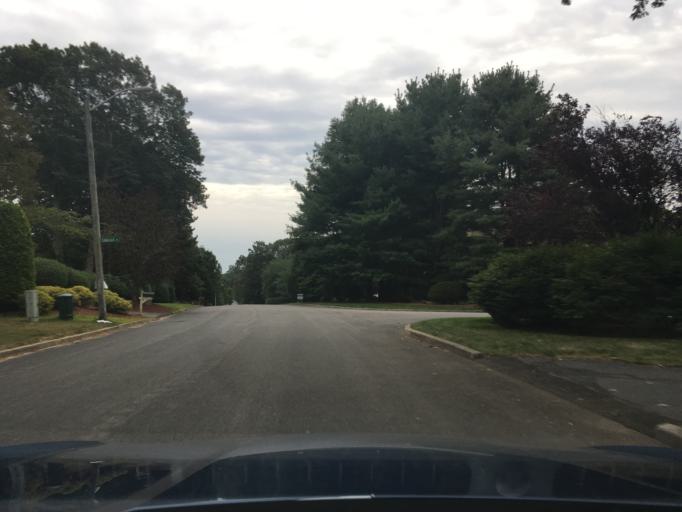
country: US
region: Rhode Island
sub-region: Kent County
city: East Greenwich
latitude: 41.6314
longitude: -71.5015
